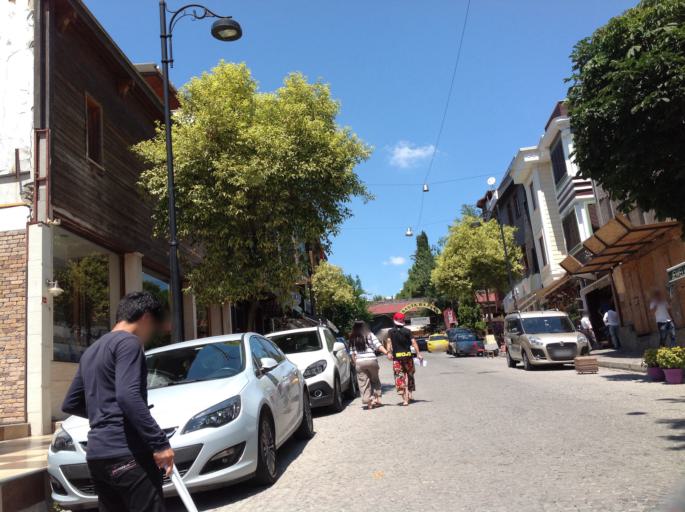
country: TR
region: Istanbul
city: Eminoenue
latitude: 41.0050
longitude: 28.9792
